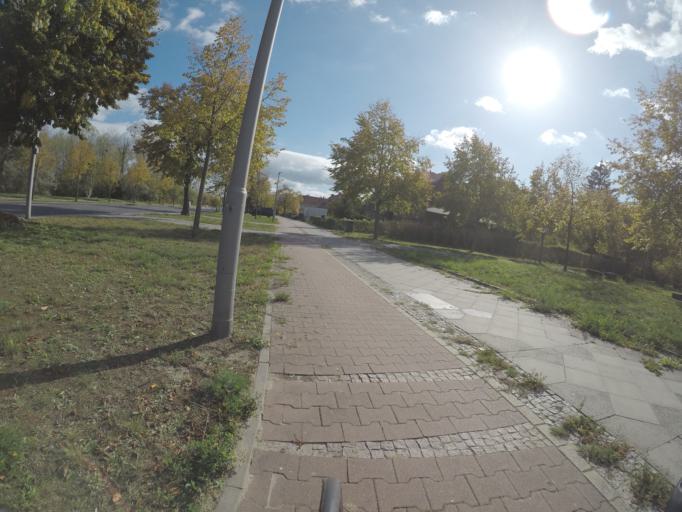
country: DE
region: Berlin
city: Staaken
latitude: 52.5357
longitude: 13.1360
